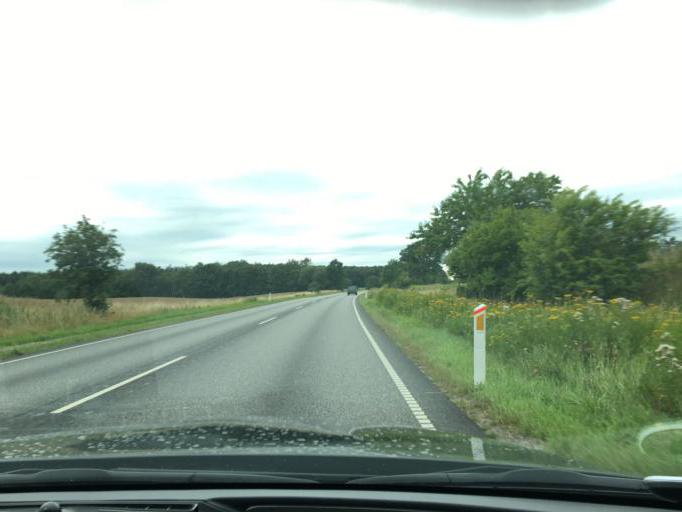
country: DK
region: Capital Region
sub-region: Horsholm Kommune
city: Horsholm
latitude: 55.8778
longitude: 12.4715
